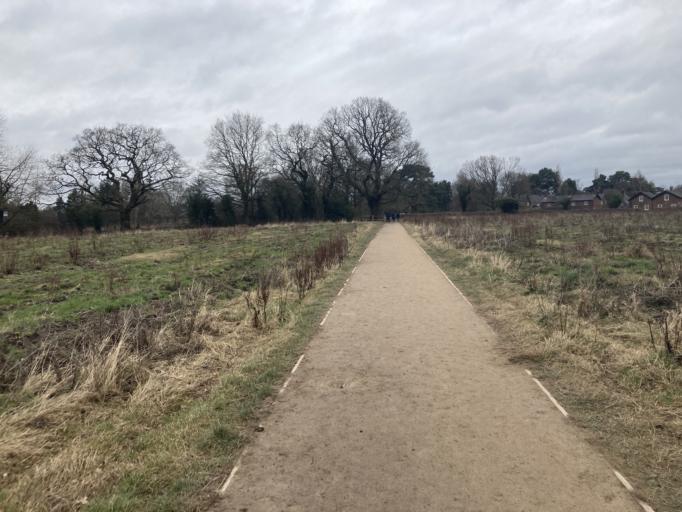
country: GB
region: England
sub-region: Cheshire East
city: Wilmslow
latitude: 53.3462
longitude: -2.2478
